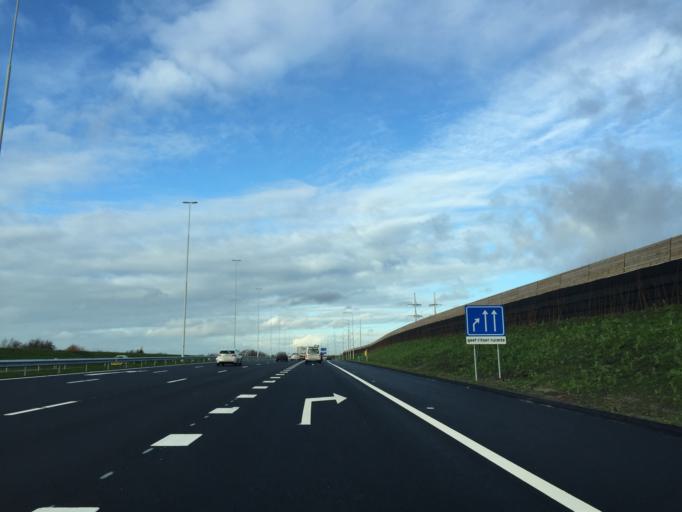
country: NL
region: South Holland
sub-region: Gemeente Delft
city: Delft
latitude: 51.9769
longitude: 4.3354
